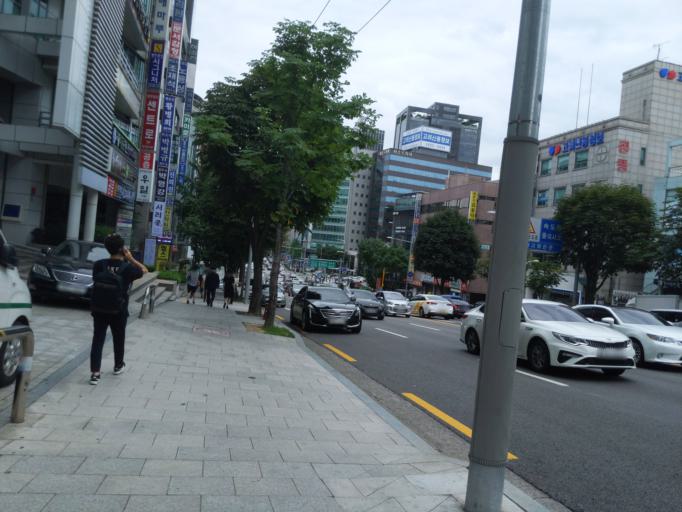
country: KR
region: Seoul
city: Seoul
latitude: 37.4952
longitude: 127.0134
